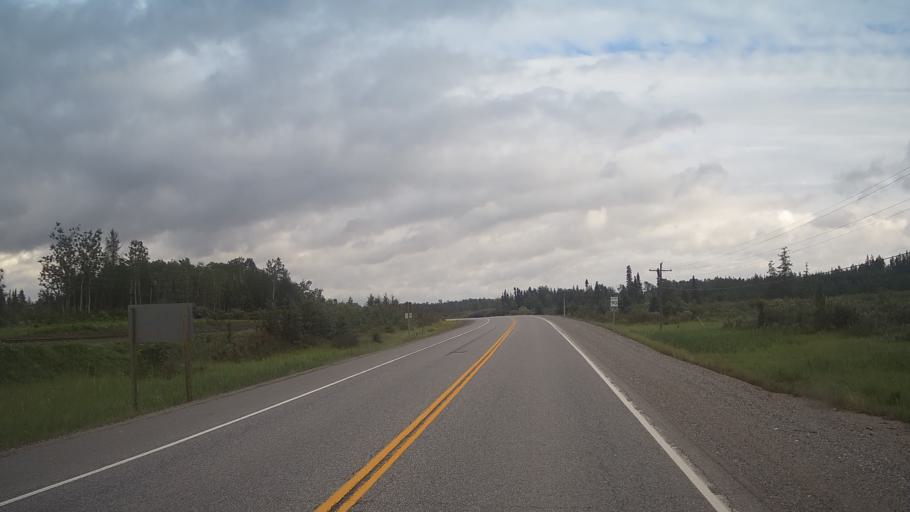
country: CA
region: Ontario
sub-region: Rainy River District
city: Atikokan
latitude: 49.0357
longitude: -90.4652
